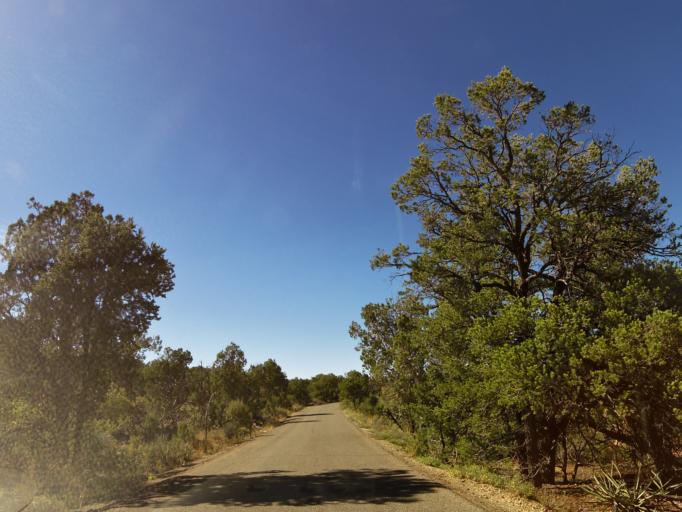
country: US
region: Colorado
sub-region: Montezuma County
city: Cortez
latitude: 37.1639
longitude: -108.4783
